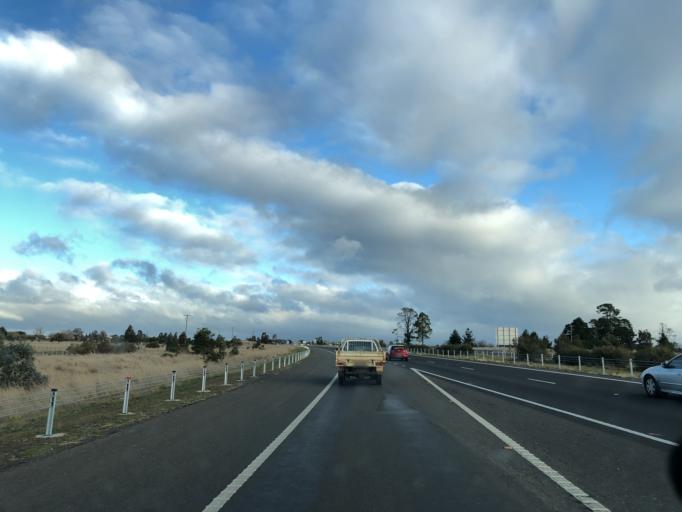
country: AU
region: Victoria
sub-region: Mount Alexander
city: Castlemaine
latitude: -37.1950
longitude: 144.4054
